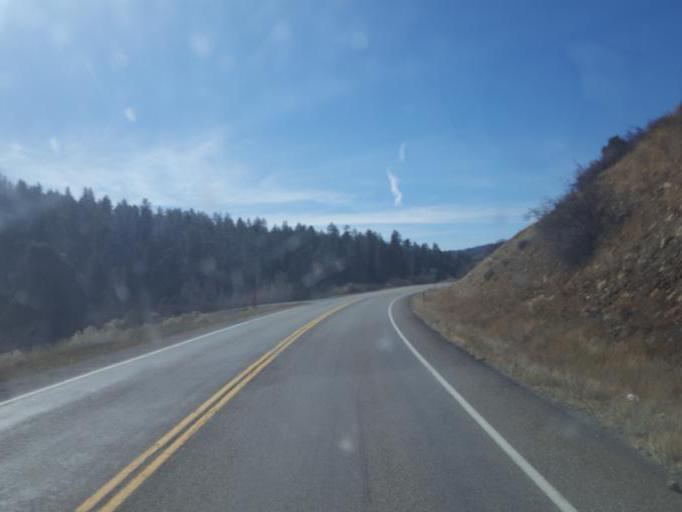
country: US
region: Colorado
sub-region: Archuleta County
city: Pagosa Springs
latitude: 37.2100
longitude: -107.2403
